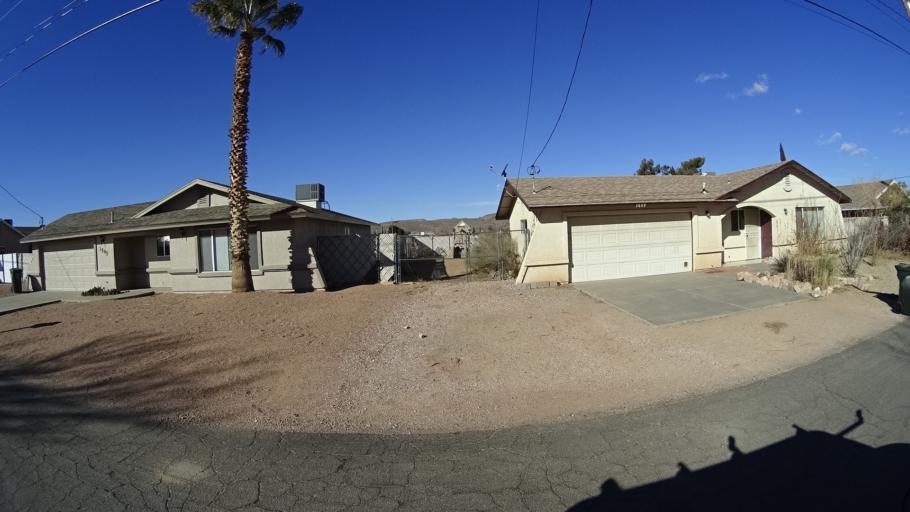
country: US
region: Arizona
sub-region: Mohave County
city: New Kingman-Butler
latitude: 35.2278
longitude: -114.0149
